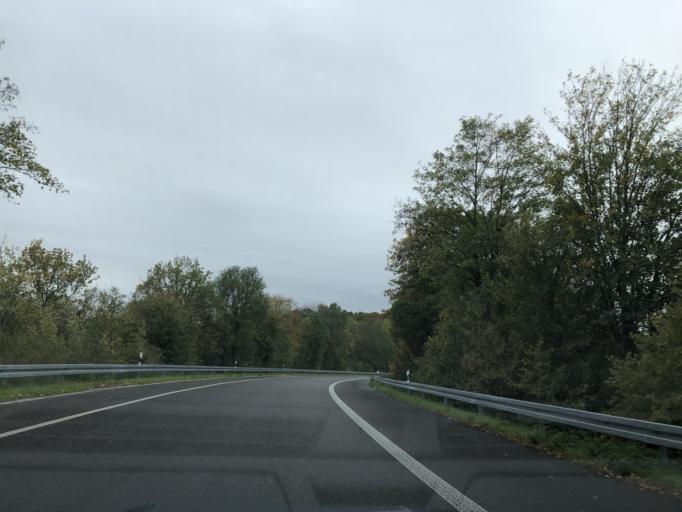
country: DE
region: North Rhine-Westphalia
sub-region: Regierungsbezirk Koln
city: Buchheim
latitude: 50.9534
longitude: 7.0344
